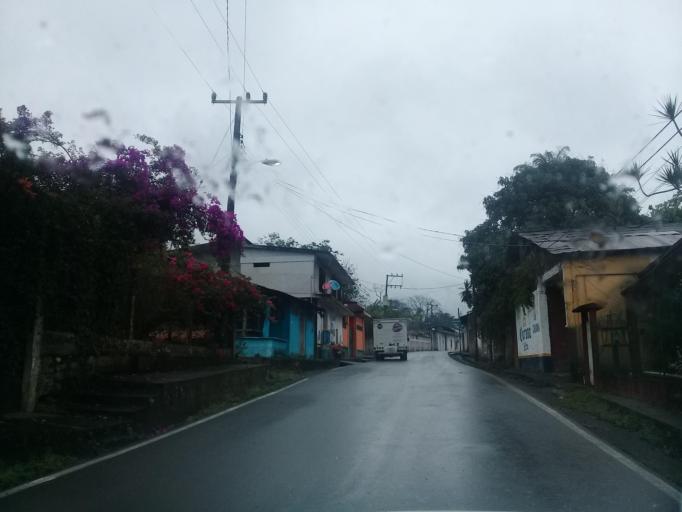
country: MX
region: Veracruz
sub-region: Amatlan de los Reyes
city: Centro de Readaptacion Social
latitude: 18.8055
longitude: -96.9554
